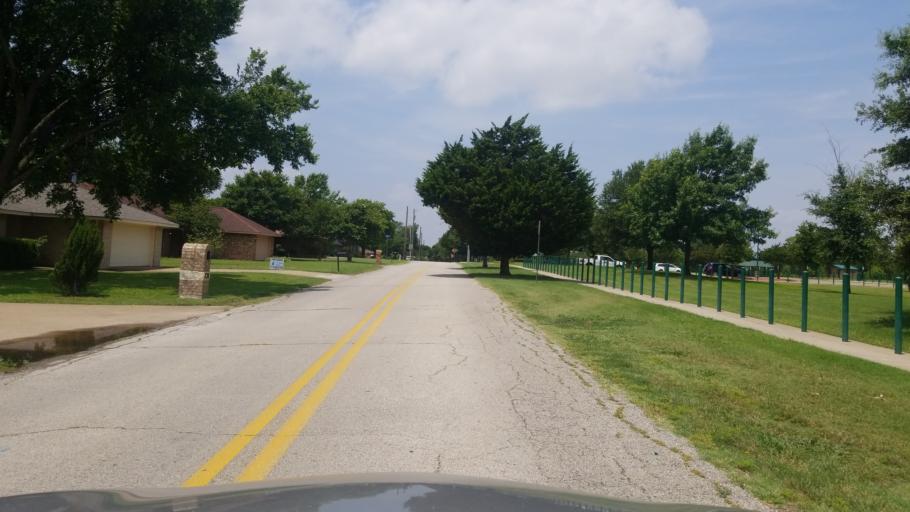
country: US
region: Texas
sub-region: Dallas County
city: Duncanville
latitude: 32.6746
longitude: -96.9122
